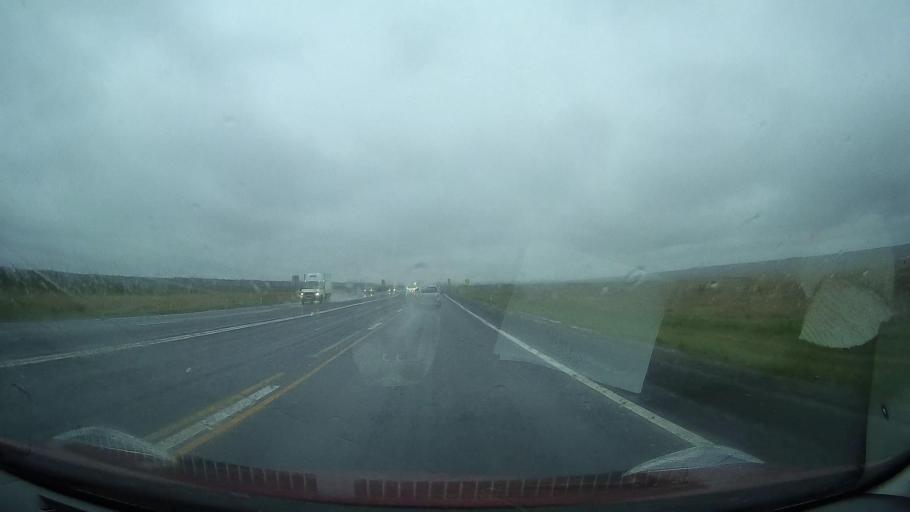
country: RU
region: Stavropol'skiy
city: Nevinnomyssk
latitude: 44.6251
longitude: 42.0613
